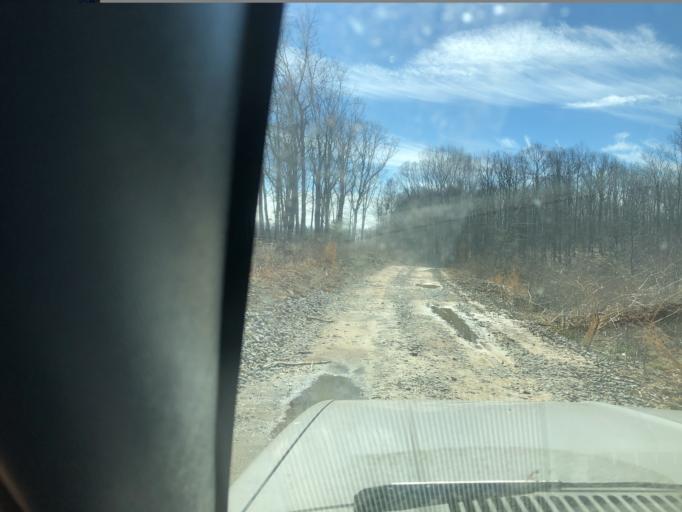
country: US
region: Tennessee
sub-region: Roane County
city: Rockwood
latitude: 35.9746
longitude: -84.7515
